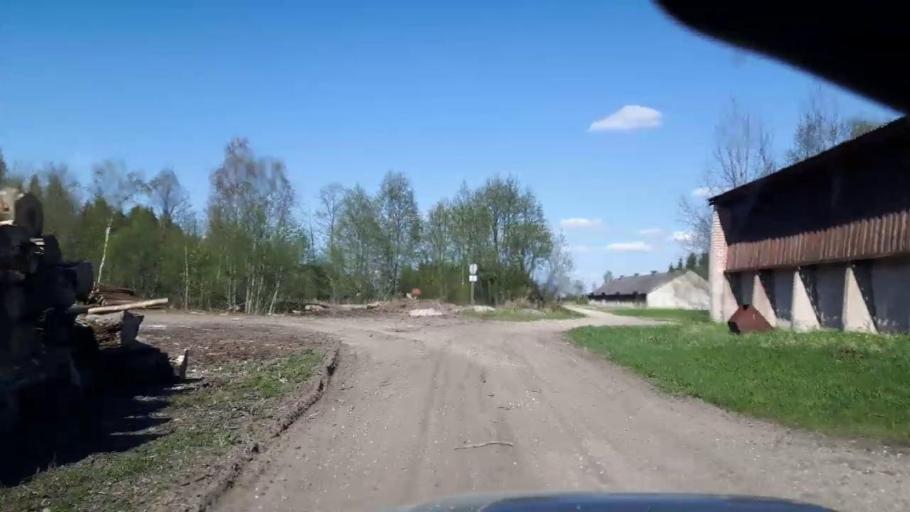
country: EE
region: Paernumaa
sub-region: Tootsi vald
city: Tootsi
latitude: 58.5235
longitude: 24.8201
